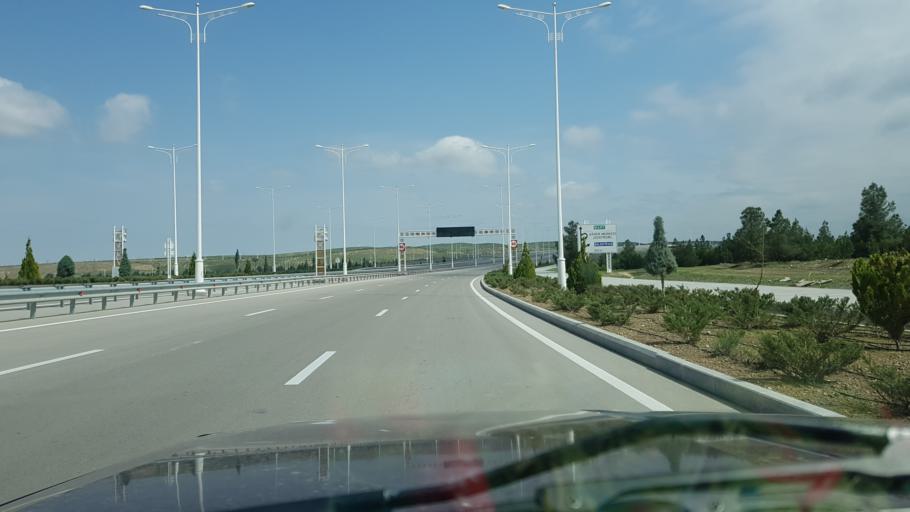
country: TM
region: Ahal
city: Ashgabat
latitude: 37.8635
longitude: 58.3679
